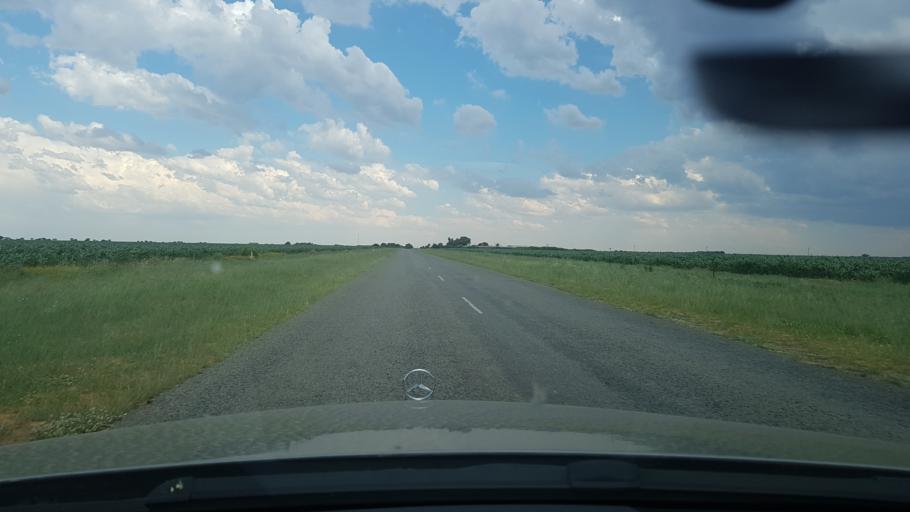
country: ZA
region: Orange Free State
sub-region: Lejweleputswa District Municipality
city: Hoopstad
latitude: -27.9120
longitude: 25.6811
